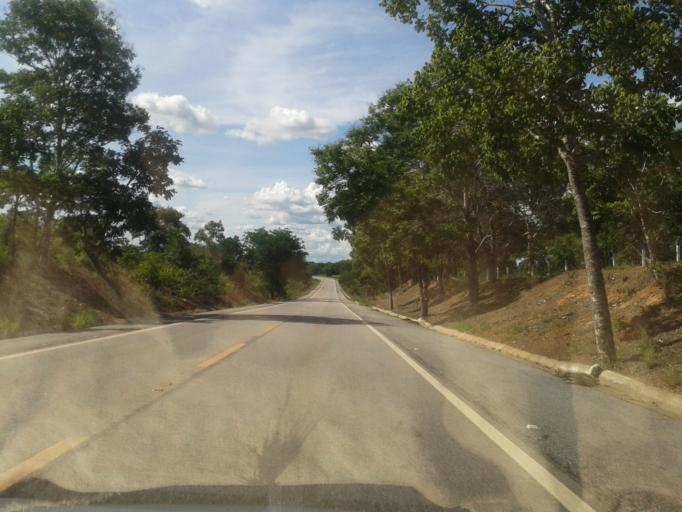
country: BR
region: Goias
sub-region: Mozarlandia
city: Mozarlandia
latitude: -15.1515
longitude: -50.5780
